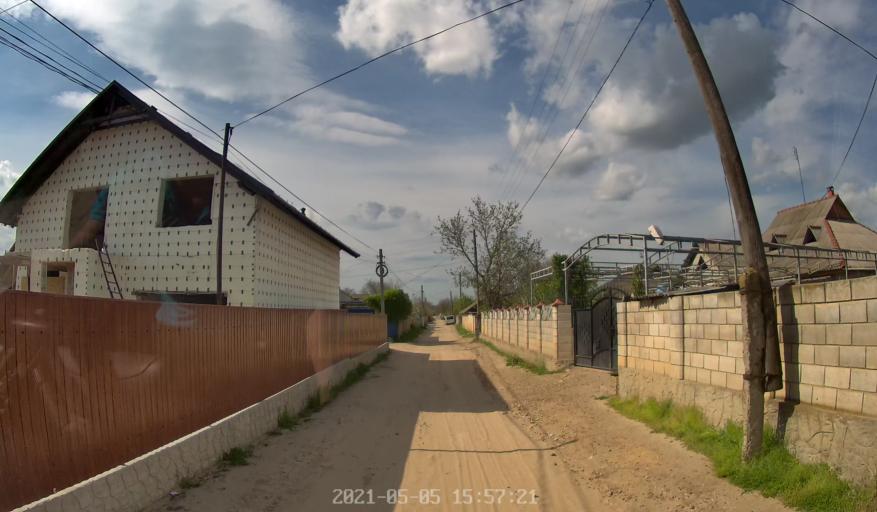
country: MD
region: Criuleni
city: Criuleni
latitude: 47.1355
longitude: 29.2058
